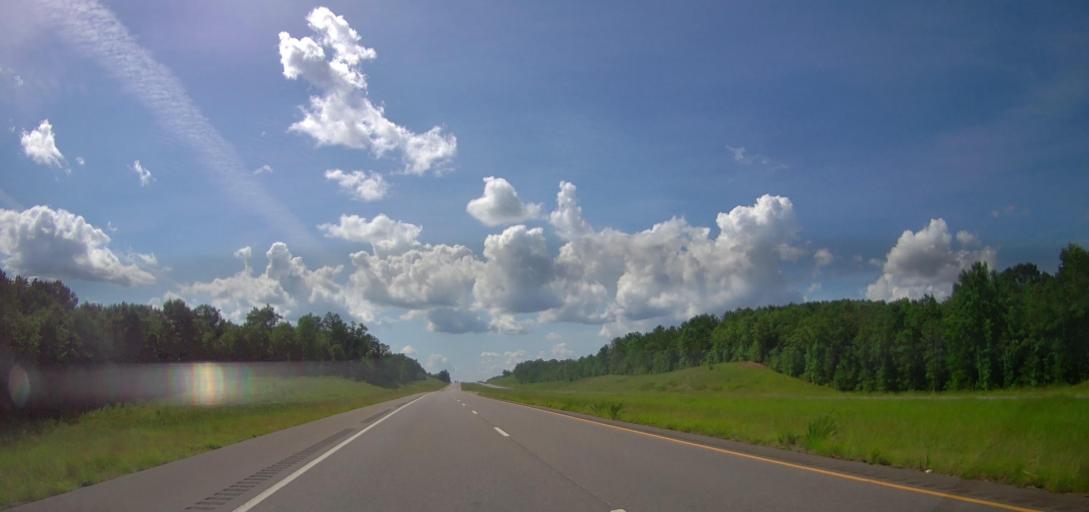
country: US
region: Alabama
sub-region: Pickens County
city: Reform
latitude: 33.3533
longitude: -87.9626
